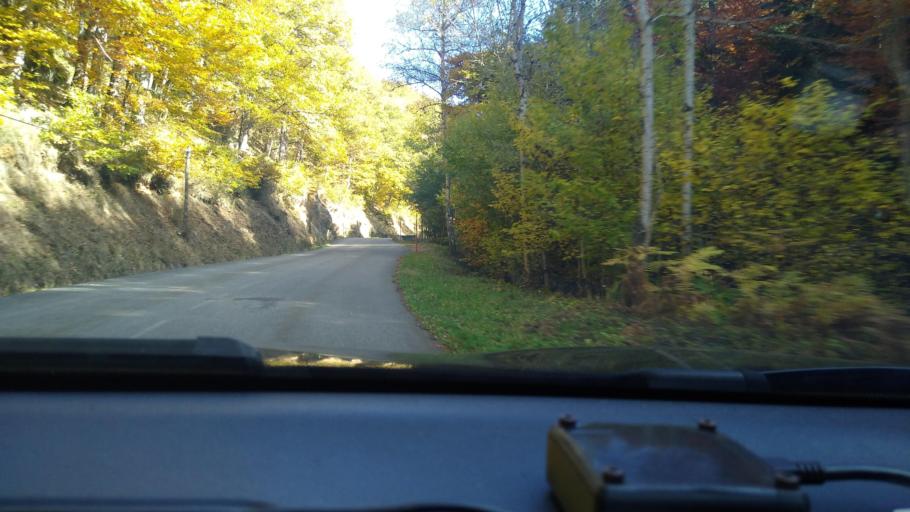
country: FR
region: Midi-Pyrenees
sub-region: Departement de l'Ariege
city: Ax-les-Thermes
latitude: 42.7188
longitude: 1.9102
